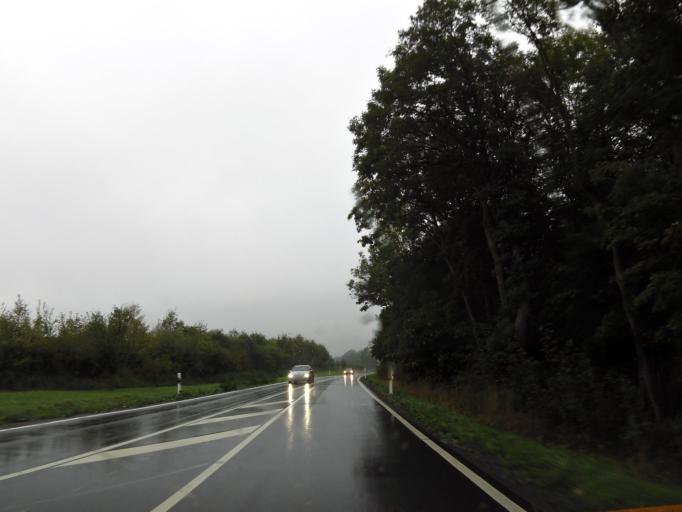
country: DE
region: Lower Saxony
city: Walkenried
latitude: 51.5935
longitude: 10.6106
